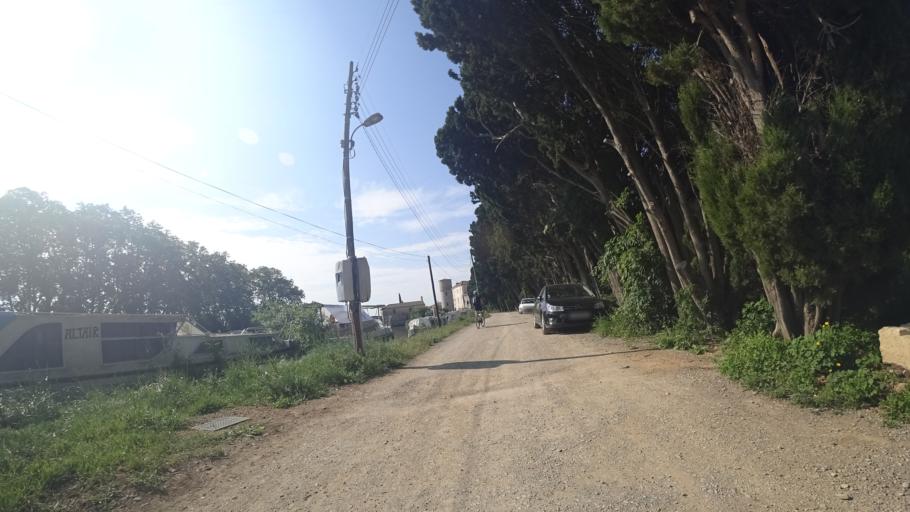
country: FR
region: Languedoc-Roussillon
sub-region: Departement de l'Aude
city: Ginestas
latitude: 43.2675
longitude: 2.9032
